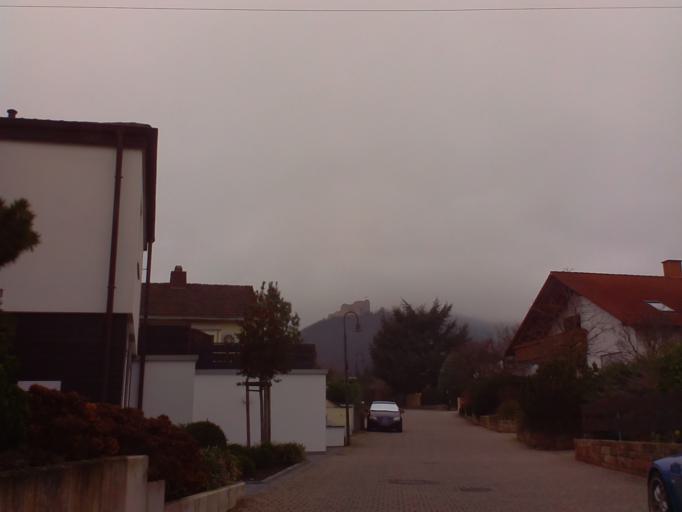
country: DE
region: Rheinland-Pfalz
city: Maikammer
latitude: 49.3208
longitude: 8.1334
